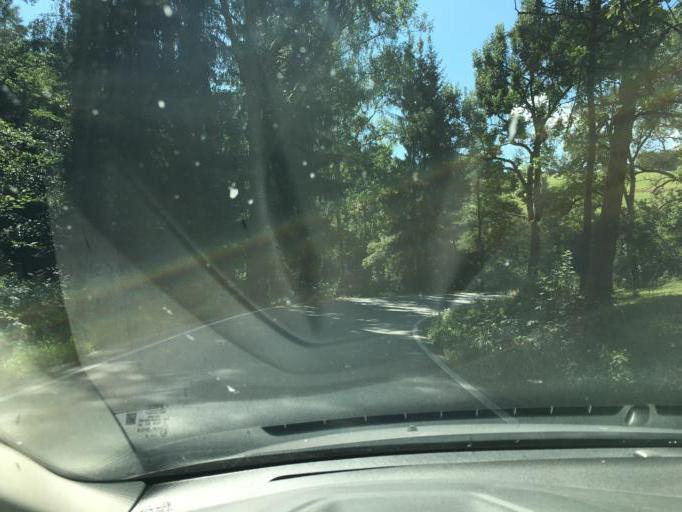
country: CZ
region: Liberecky
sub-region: Okres Semily
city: Vysoke nad Jizerou
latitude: 50.7028
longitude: 15.3657
